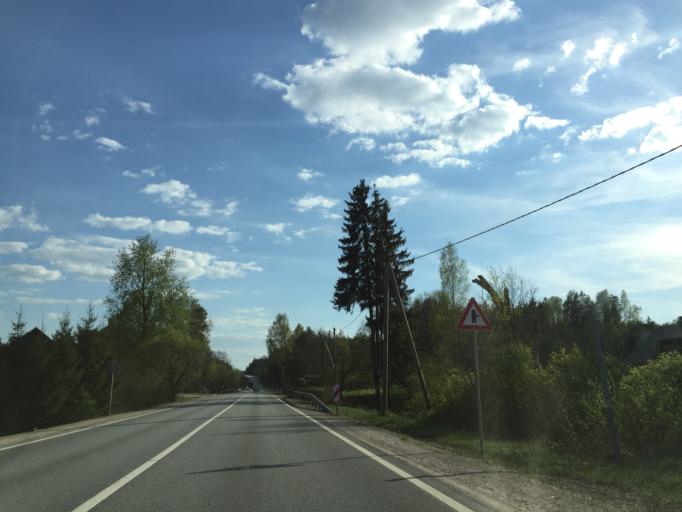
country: LV
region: Pargaujas
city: Stalbe
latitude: 57.2953
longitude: 24.9223
